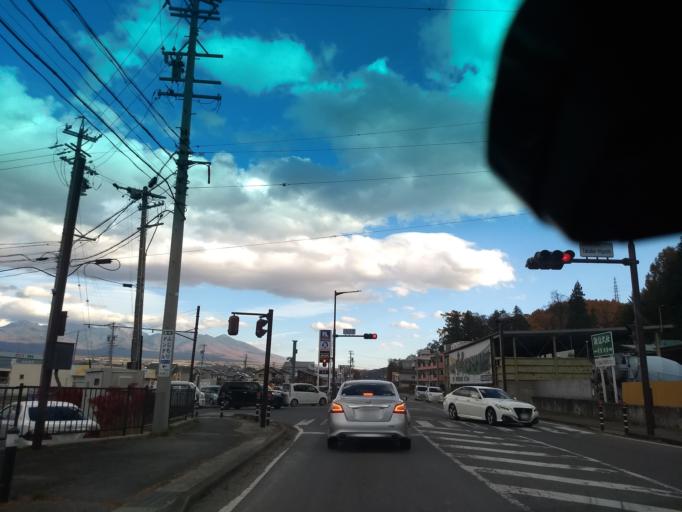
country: JP
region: Nagano
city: Chino
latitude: 35.9944
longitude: 138.1326
